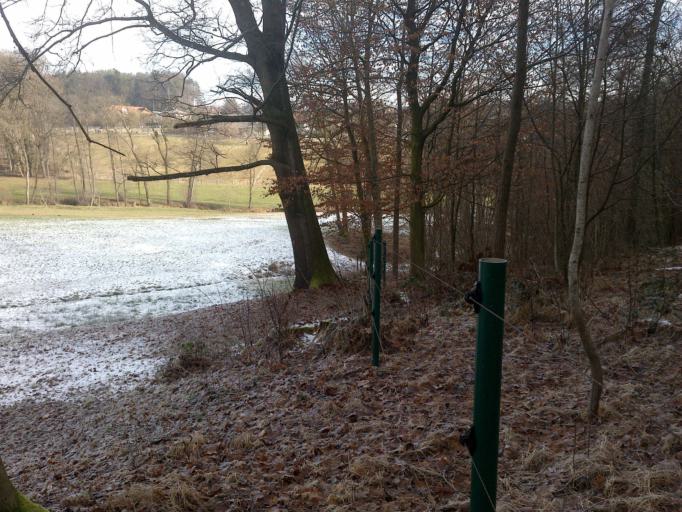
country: AT
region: Styria
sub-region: Politischer Bezirk Graz-Umgebung
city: Hart bei Graz
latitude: 47.0519
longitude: 15.5067
